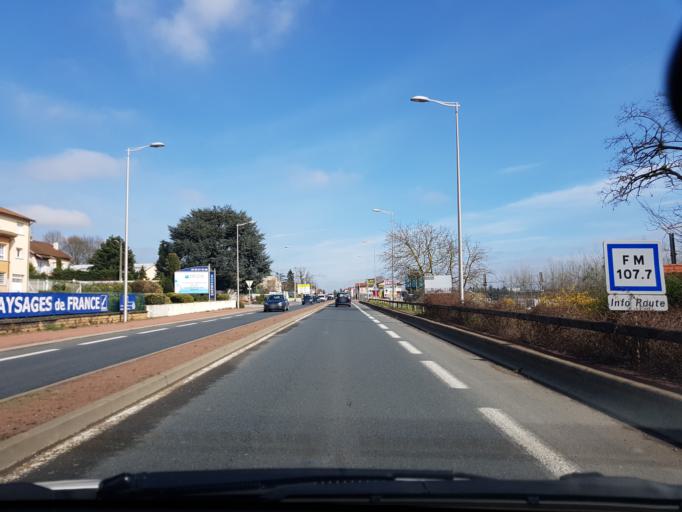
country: FR
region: Rhone-Alpes
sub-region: Departement du Rhone
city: Villefranche-sur-Saone
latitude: 45.9662
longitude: 4.7164
